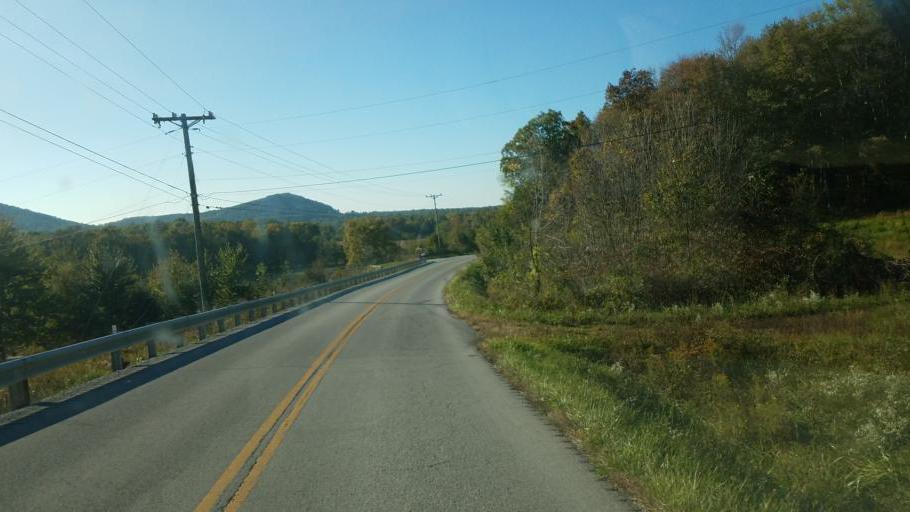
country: US
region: Kentucky
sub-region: Fleming County
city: Flemingsburg
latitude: 38.4671
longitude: -83.5743
